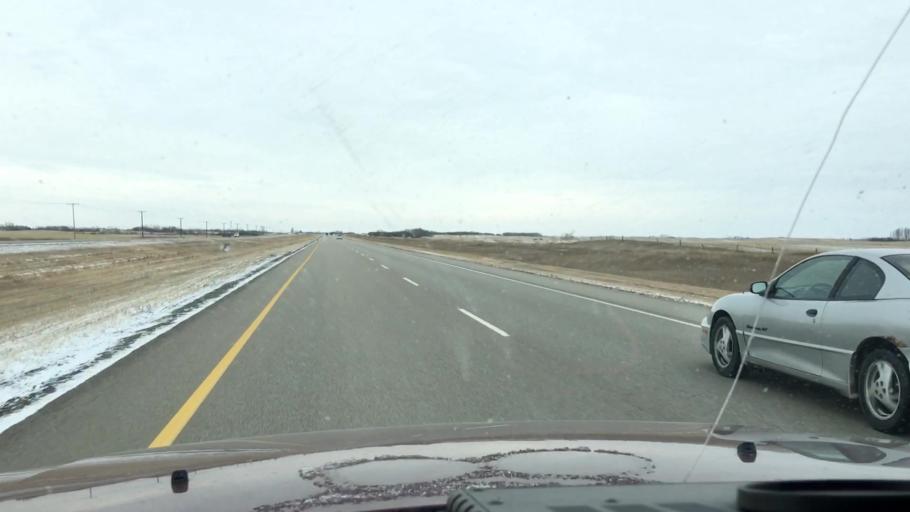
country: CA
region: Saskatchewan
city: Watrous
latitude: 51.4021
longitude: -106.1781
